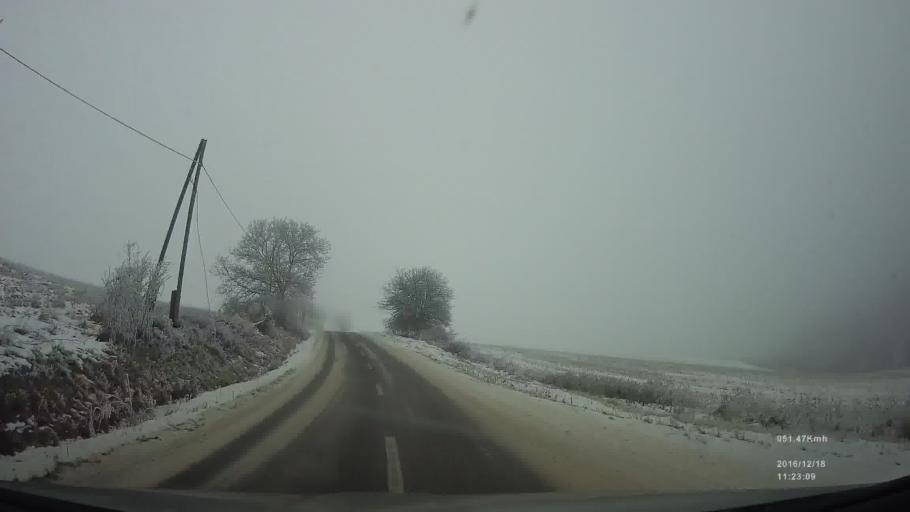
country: SK
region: Presovsky
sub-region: Okres Presov
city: Presov
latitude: 48.8963
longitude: 21.3855
